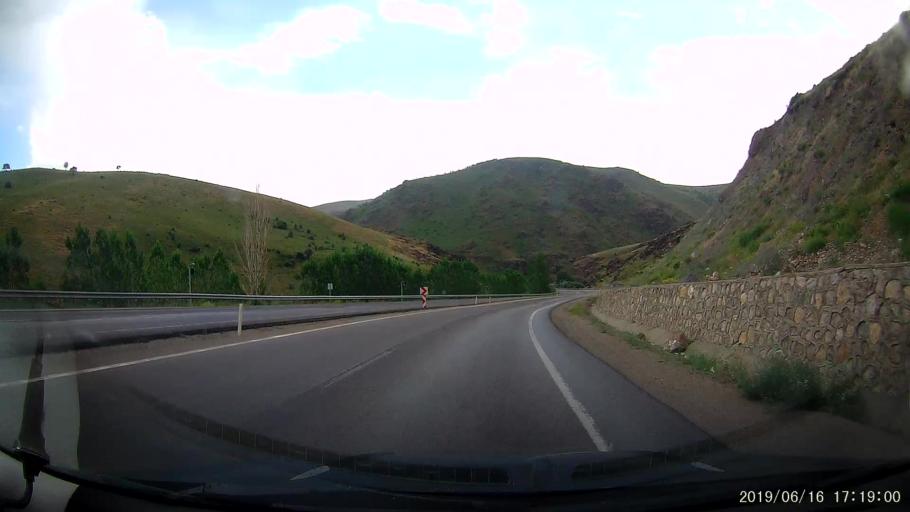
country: TR
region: Erzincan
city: Tercan
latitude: 39.8059
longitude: 40.5316
